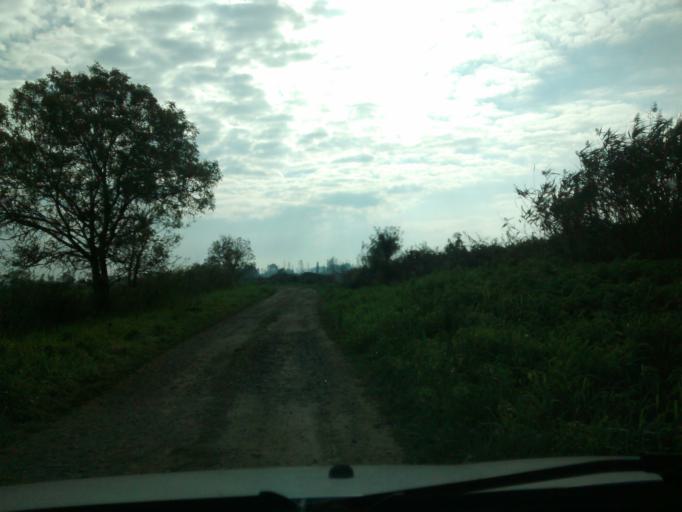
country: FR
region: Pays de la Loire
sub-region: Departement de la Loire-Atlantique
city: Cordemais
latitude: 47.2463
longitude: -1.8714
